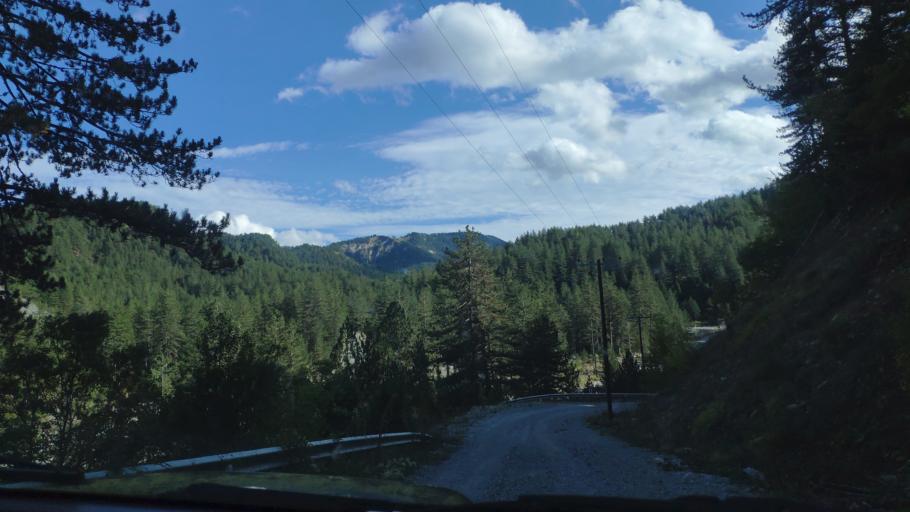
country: AL
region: Korce
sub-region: Rrethi i Devollit
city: Miras
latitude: 40.4126
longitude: 20.8731
